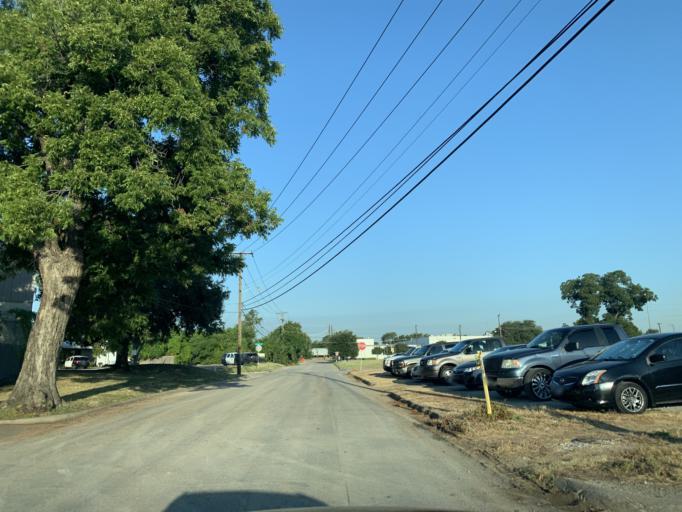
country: US
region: Texas
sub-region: Tarrant County
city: Fort Worth
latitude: 32.7569
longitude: -97.3463
